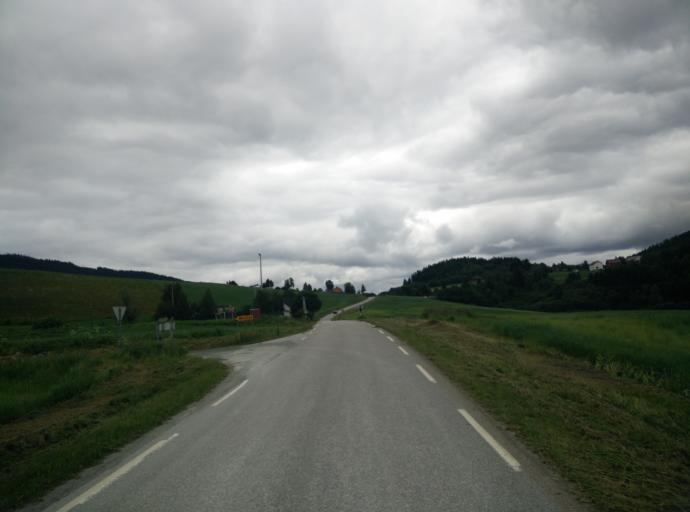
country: NO
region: Sor-Trondelag
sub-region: Skaun
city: Borsa
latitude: 63.3178
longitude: 10.0773
